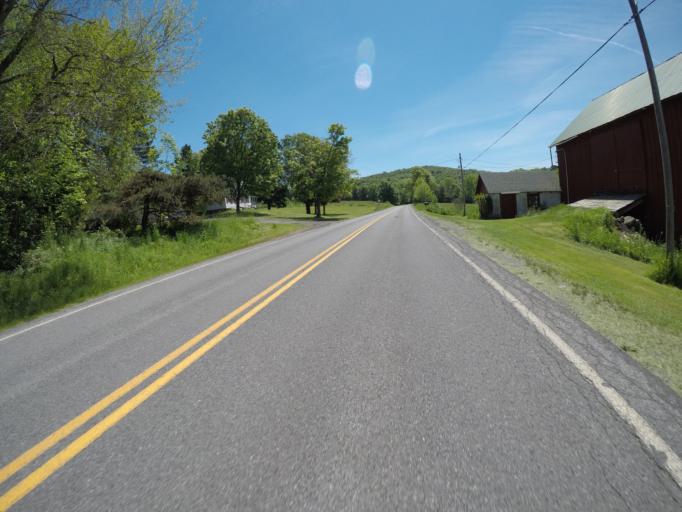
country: US
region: New York
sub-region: Delaware County
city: Delhi
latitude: 42.2088
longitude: -74.8565
